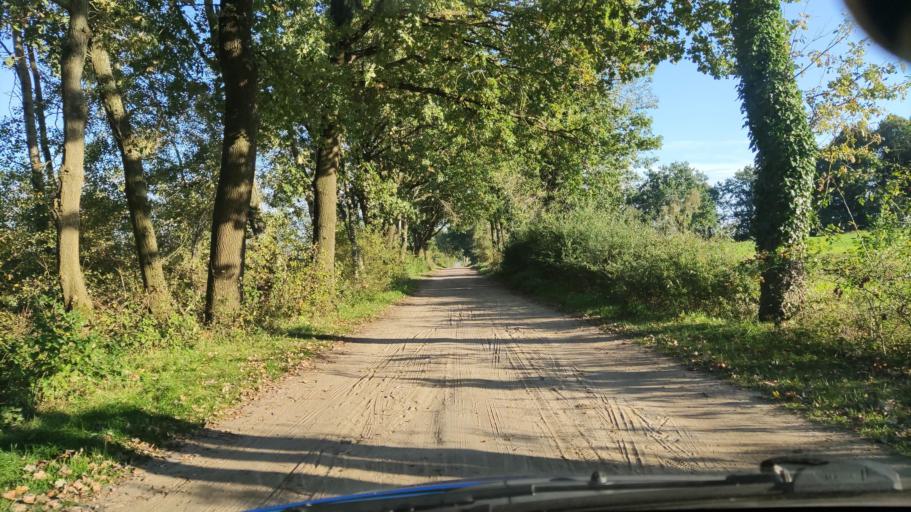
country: DE
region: Lower Saxony
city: Sudergellersen
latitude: 53.2156
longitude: 10.2779
